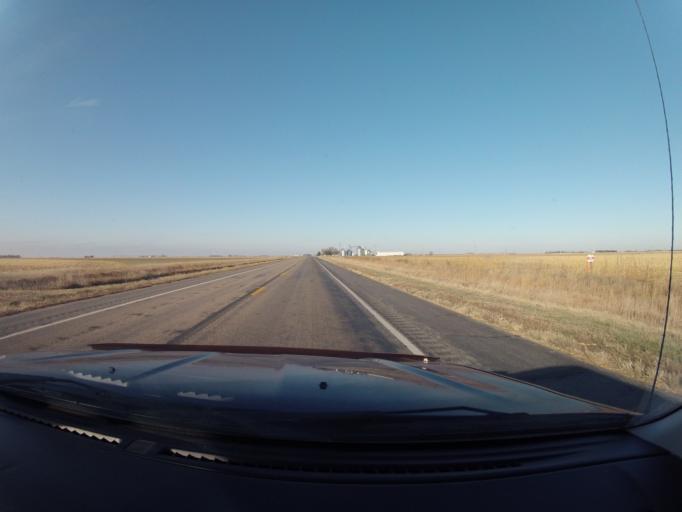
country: US
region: Nebraska
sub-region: Kearney County
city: Minden
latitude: 40.5224
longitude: -98.9518
